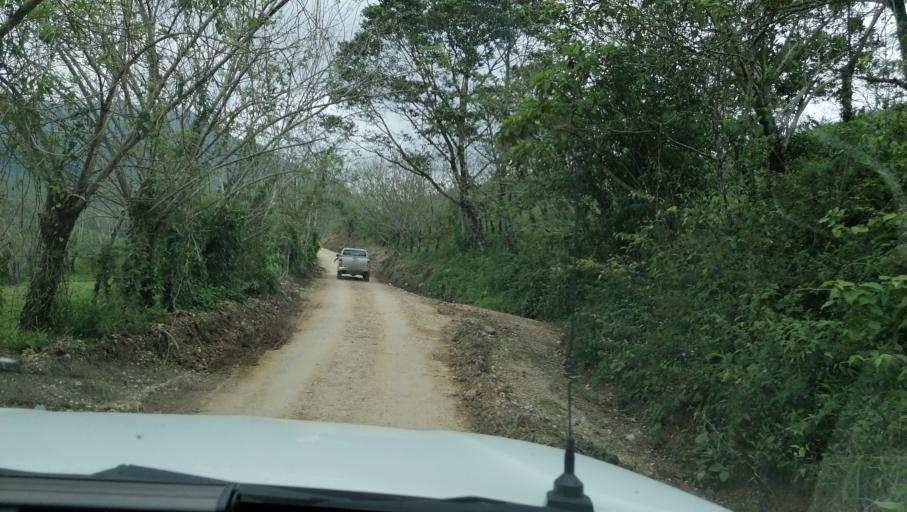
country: MX
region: Chiapas
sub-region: Ocotepec
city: San Pablo Huacano
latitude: 17.2683
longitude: -93.2563
